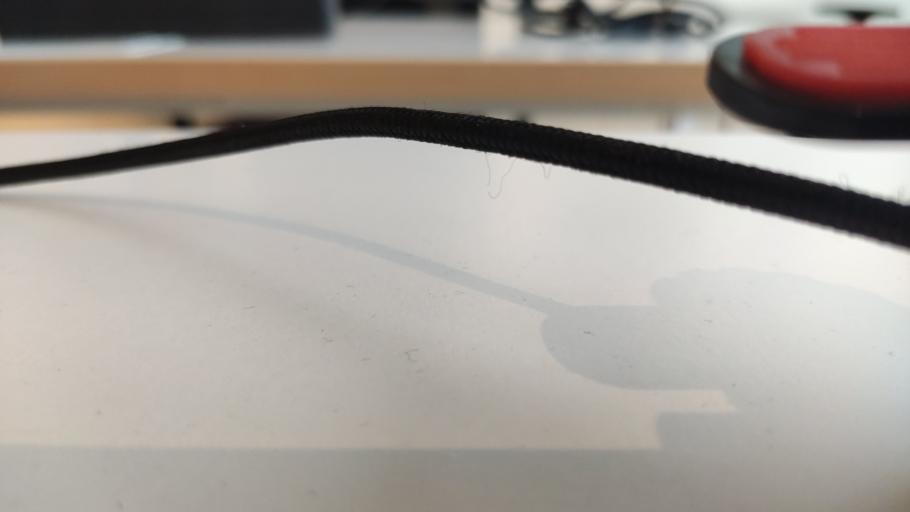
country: RU
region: Moskovskaya
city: Klin
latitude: 56.3651
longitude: 36.7671
